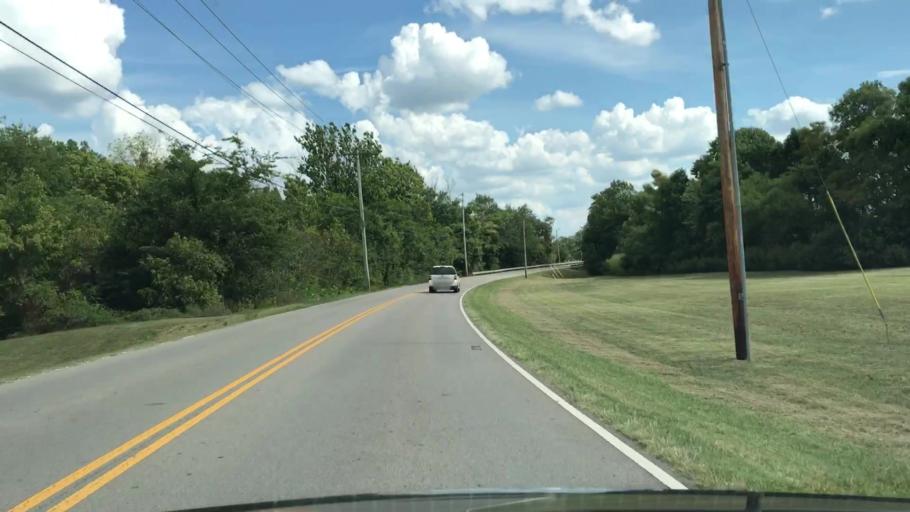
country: US
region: Tennessee
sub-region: Maury County
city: Spring Hill
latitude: 35.7427
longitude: -86.9263
